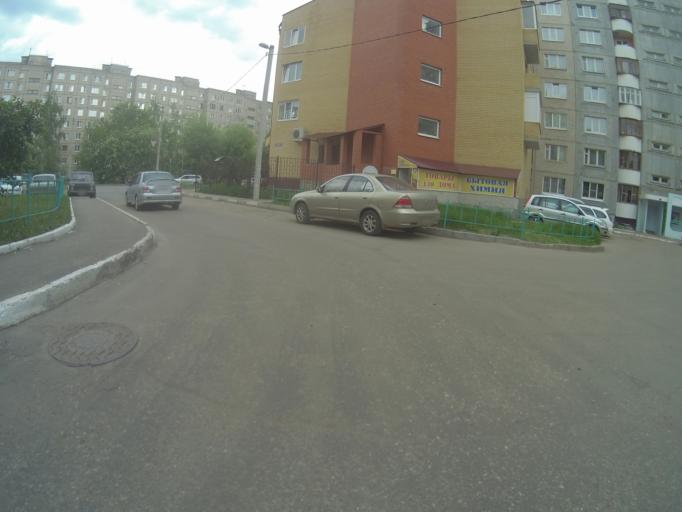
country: RU
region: Vladimir
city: Kommunar
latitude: 56.1622
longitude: 40.4636
